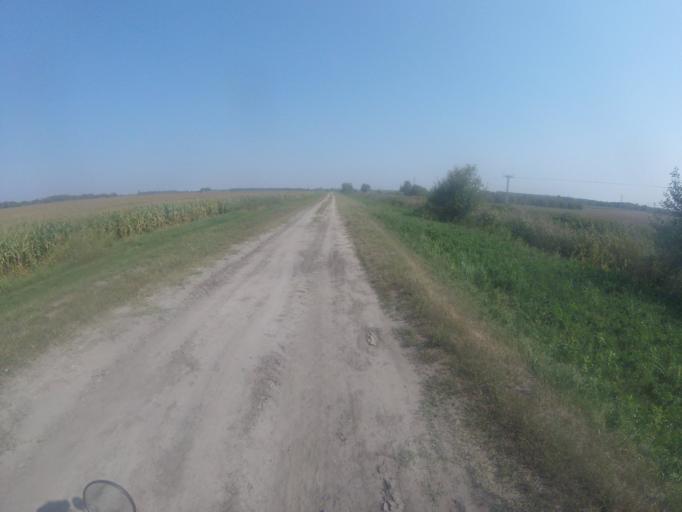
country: HU
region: Bacs-Kiskun
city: Ersekcsanad
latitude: 46.2208
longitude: 18.9565
